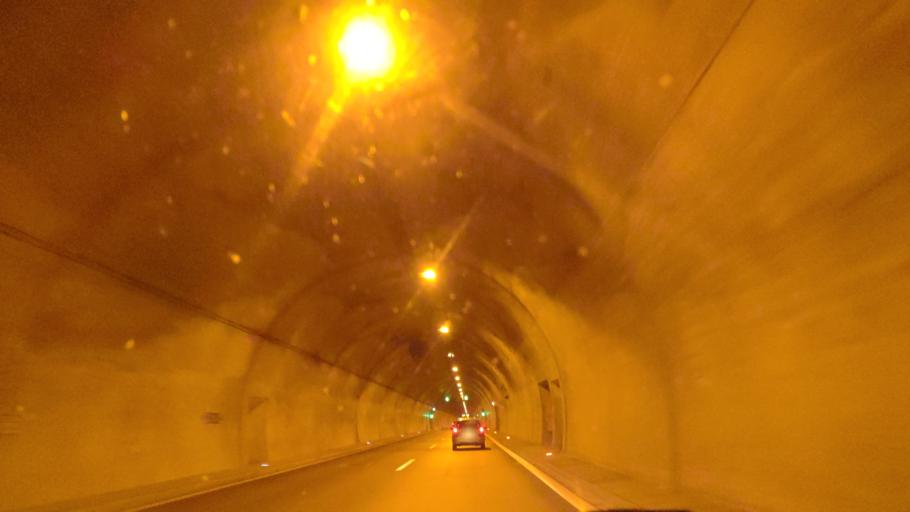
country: GR
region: Epirus
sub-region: Nomos Ioanninon
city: Katsikas
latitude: 39.6939
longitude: 20.9672
